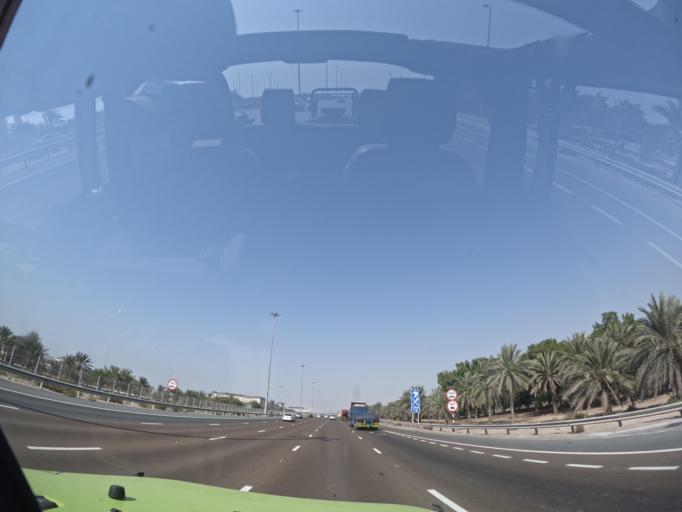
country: AE
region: Abu Dhabi
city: Abu Dhabi
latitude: 24.5154
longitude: 54.6678
